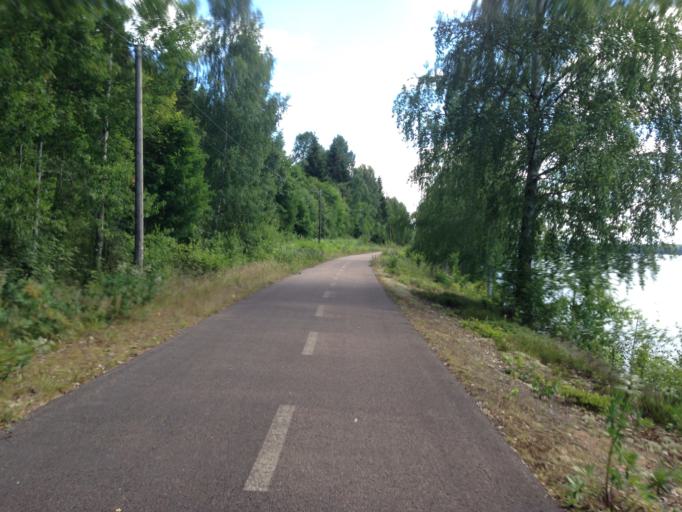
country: SE
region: Dalarna
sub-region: Ludvika Kommun
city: Grangesberg
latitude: 60.2320
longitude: 15.0310
